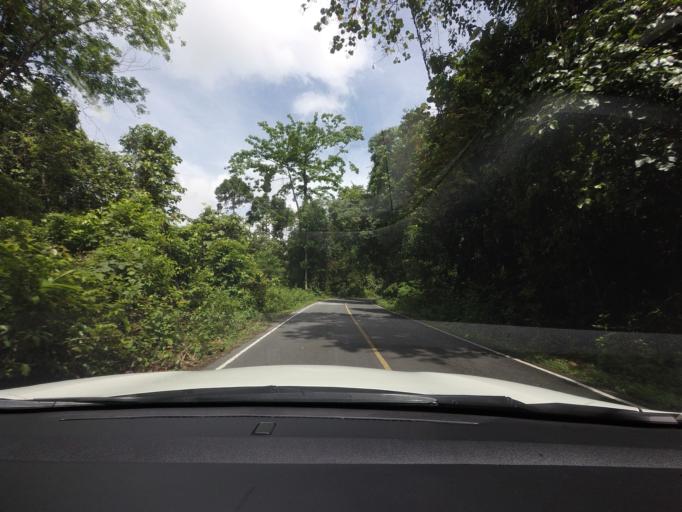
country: TH
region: Nakhon Nayok
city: Pak Phli
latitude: 14.3104
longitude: 101.3797
